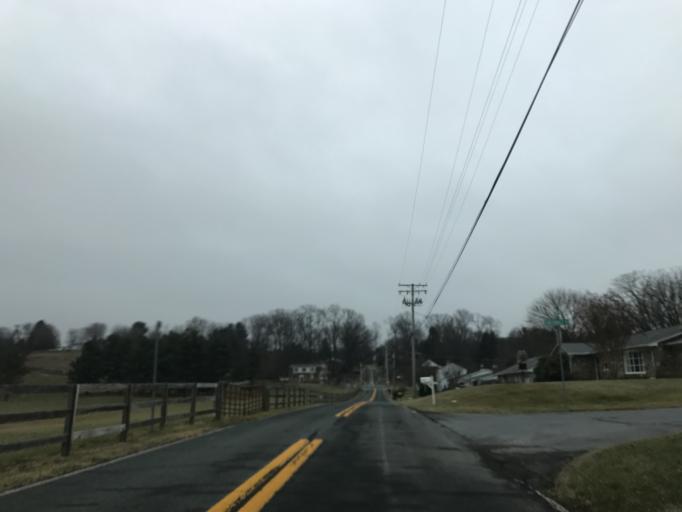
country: US
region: Maryland
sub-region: Carroll County
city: Westminster
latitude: 39.5543
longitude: -76.9967
